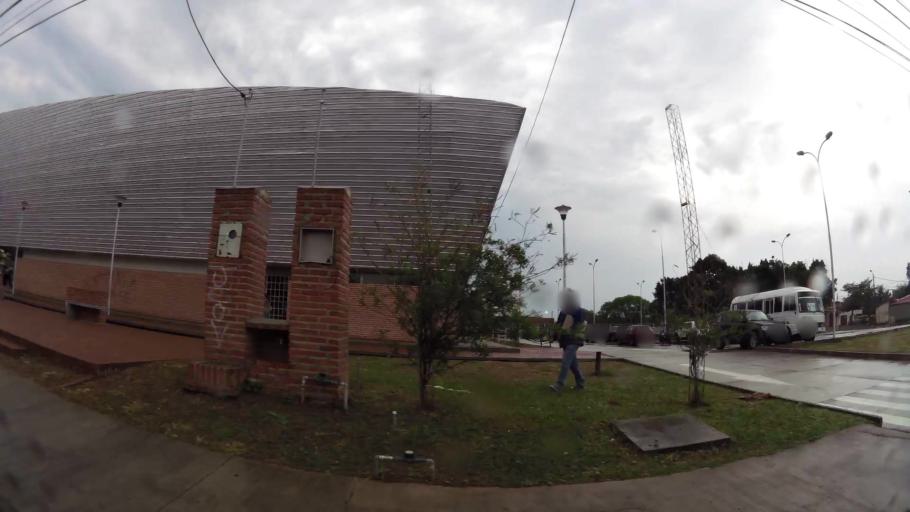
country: BO
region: Santa Cruz
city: Santa Cruz de la Sierra
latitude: -17.7659
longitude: -63.1529
